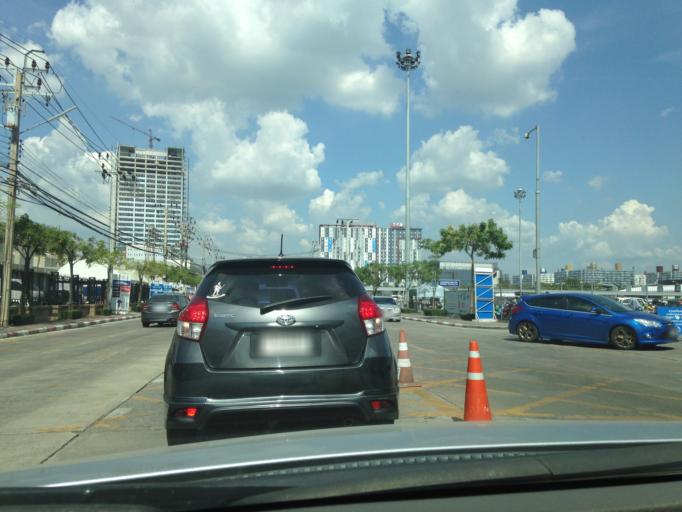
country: TH
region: Bangkok
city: Lak Si
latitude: 13.9121
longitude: 100.5498
